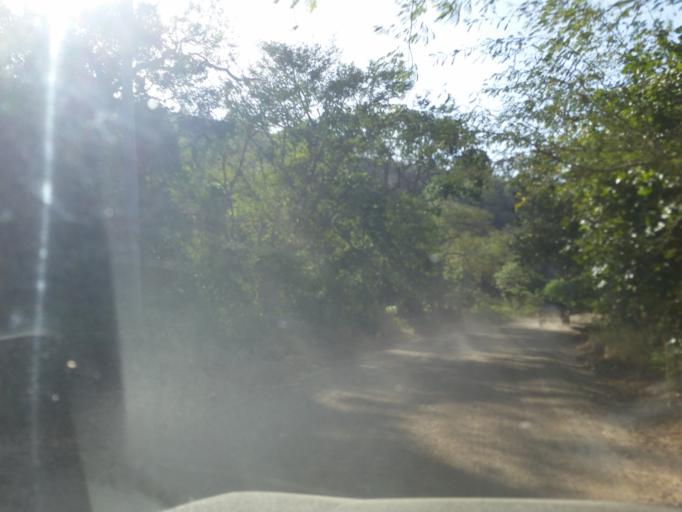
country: NI
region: Rivas
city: San Juan del Sur
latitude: 11.1890
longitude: -85.8082
